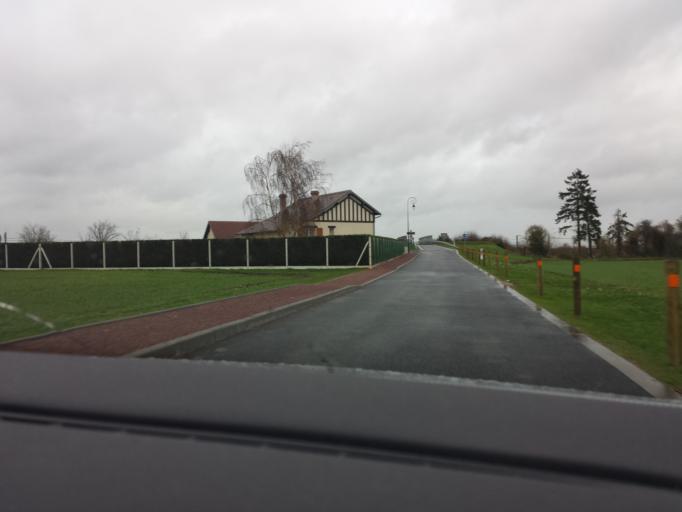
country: FR
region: Haute-Normandie
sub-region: Departement de l'Eure
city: Evreux
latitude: 49.0051
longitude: 1.2013
